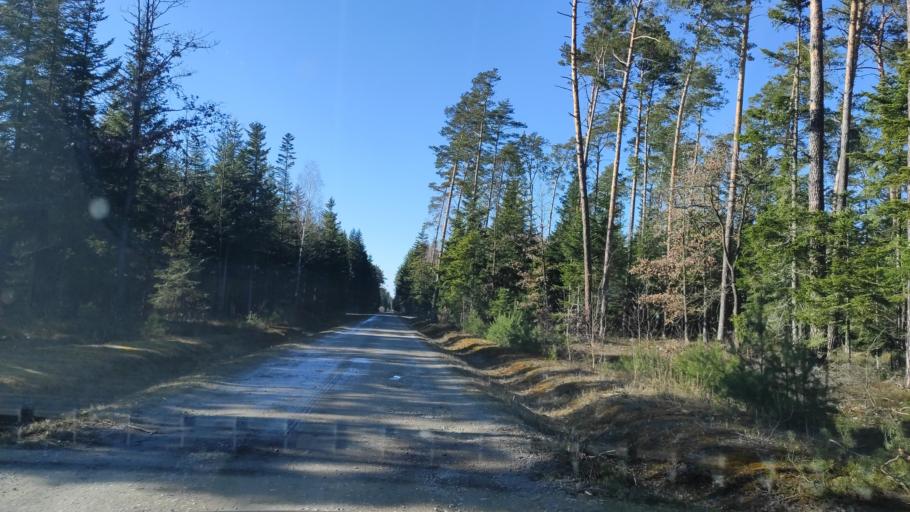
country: PL
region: Masovian Voivodeship
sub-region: Powiat radomski
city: Jedlnia-Letnisko
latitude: 51.4651
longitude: 21.3175
